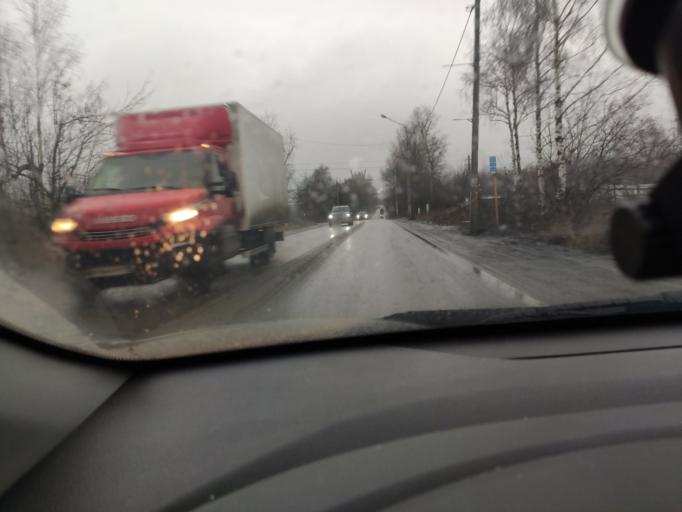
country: RU
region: Moskovskaya
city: Biryulevo Zapadnoye
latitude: 55.5698
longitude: 37.6492
